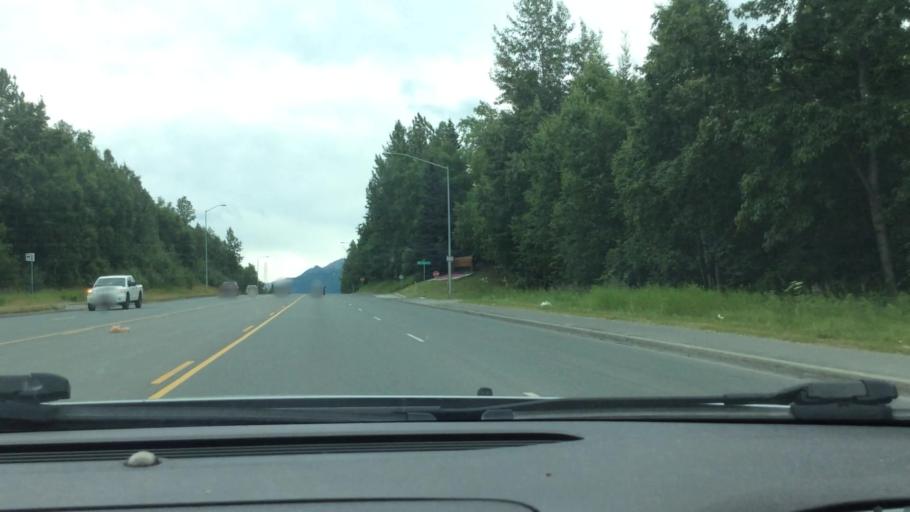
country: US
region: Alaska
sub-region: Anchorage Municipality
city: Anchorage
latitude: 61.2096
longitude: -149.7881
